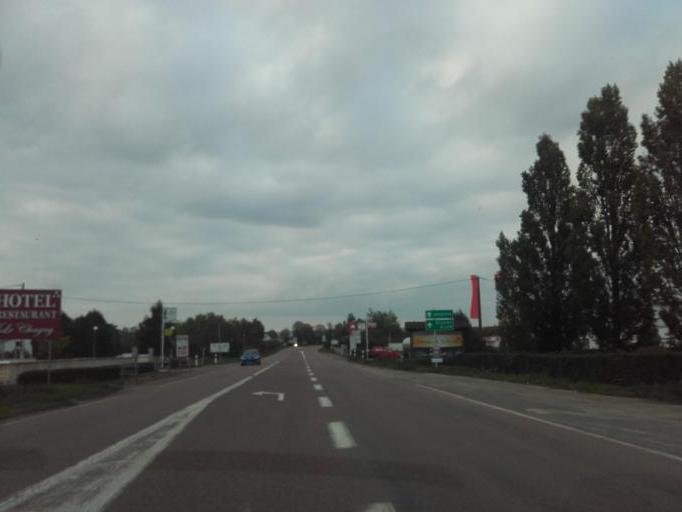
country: FR
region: Bourgogne
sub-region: Departement de Saone-et-Loire
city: Chagny
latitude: 46.8968
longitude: 4.7624
